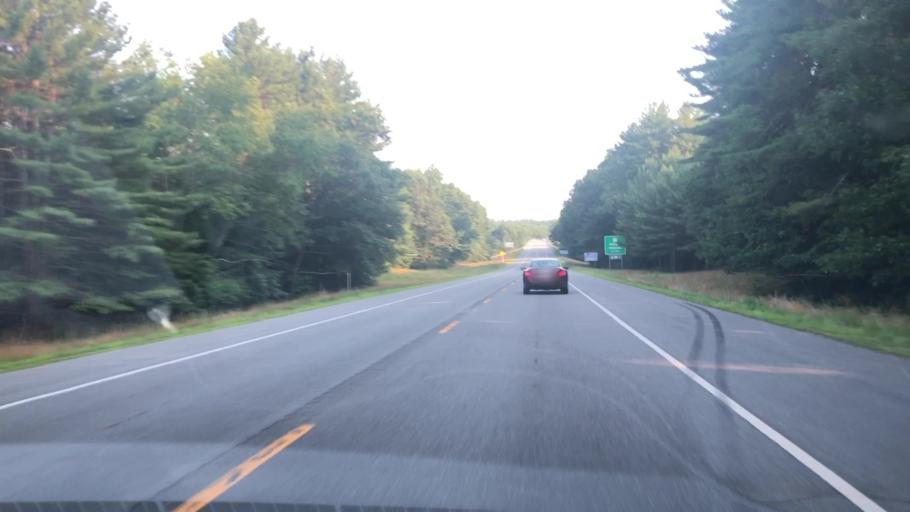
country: US
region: New Hampshire
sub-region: Hillsborough County
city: Milford
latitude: 42.8328
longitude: -71.6182
